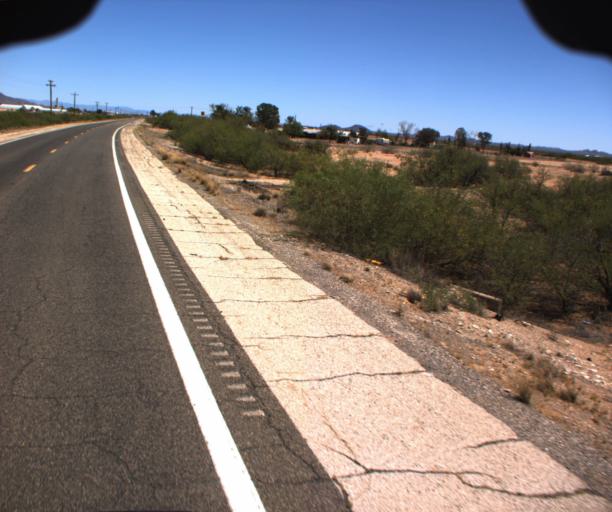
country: US
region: Arizona
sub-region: Yavapai County
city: Congress
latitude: 33.9383
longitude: -113.1957
